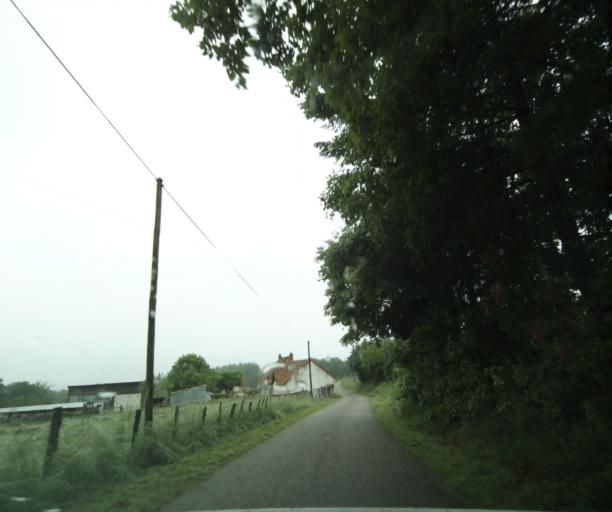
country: FR
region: Bourgogne
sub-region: Departement de Saone-et-Loire
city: Charolles
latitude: 46.4217
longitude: 4.3730
